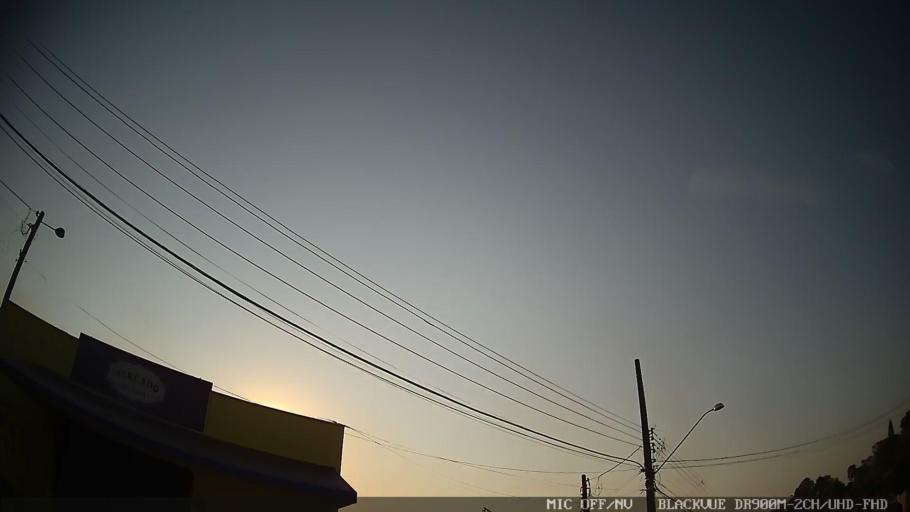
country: BR
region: Sao Paulo
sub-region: Itatiba
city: Itatiba
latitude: -23.0050
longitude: -46.8196
